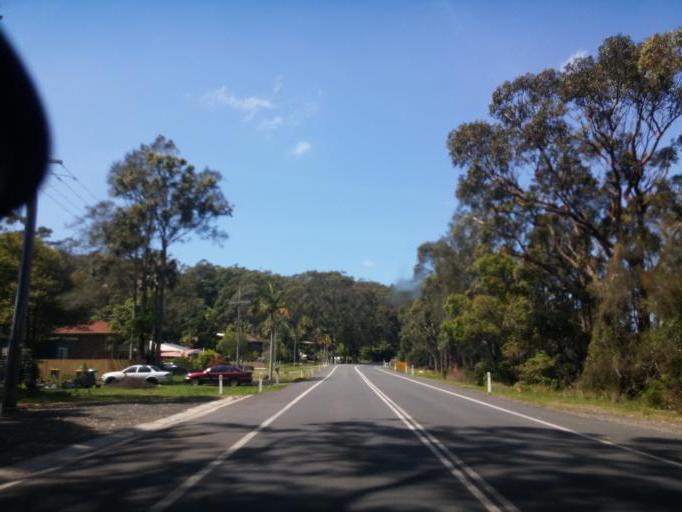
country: AU
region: New South Wales
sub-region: Great Lakes
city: Forster
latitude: -32.3690
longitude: 152.4796
